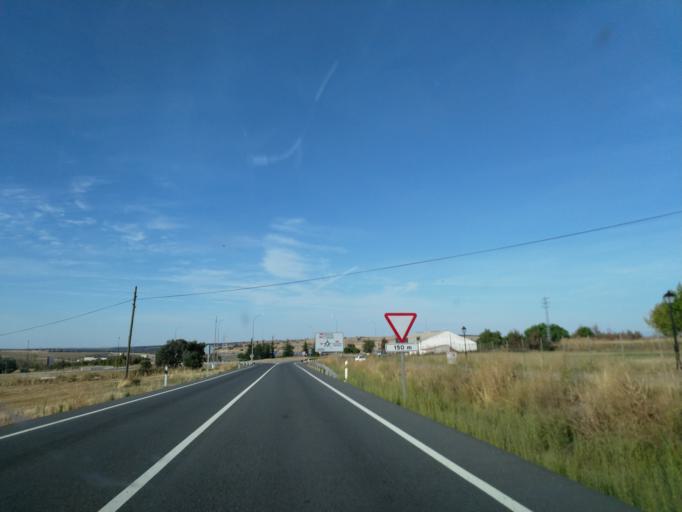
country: ES
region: Castille and Leon
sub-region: Provincia de Segovia
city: Villacastin
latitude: 40.7809
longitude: -4.4218
